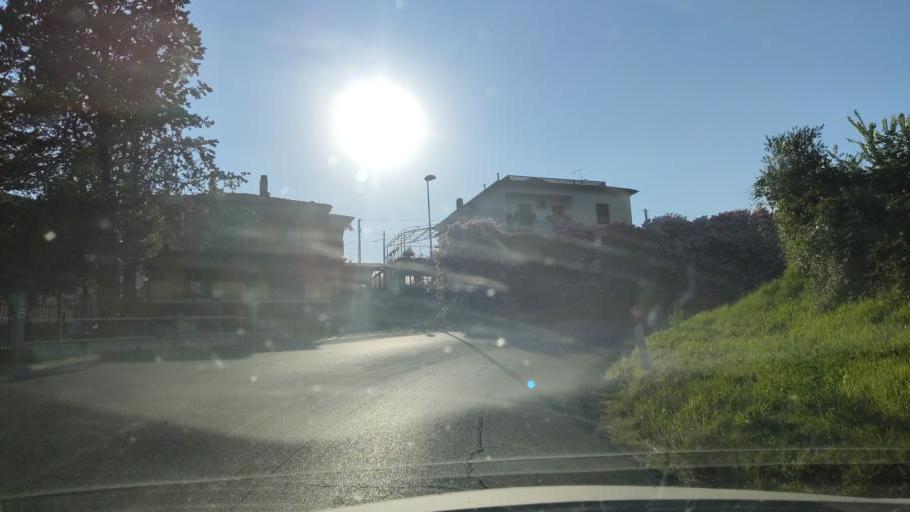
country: IT
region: Umbria
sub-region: Provincia di Terni
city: Narni Scalo
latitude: 42.5378
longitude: 12.5142
